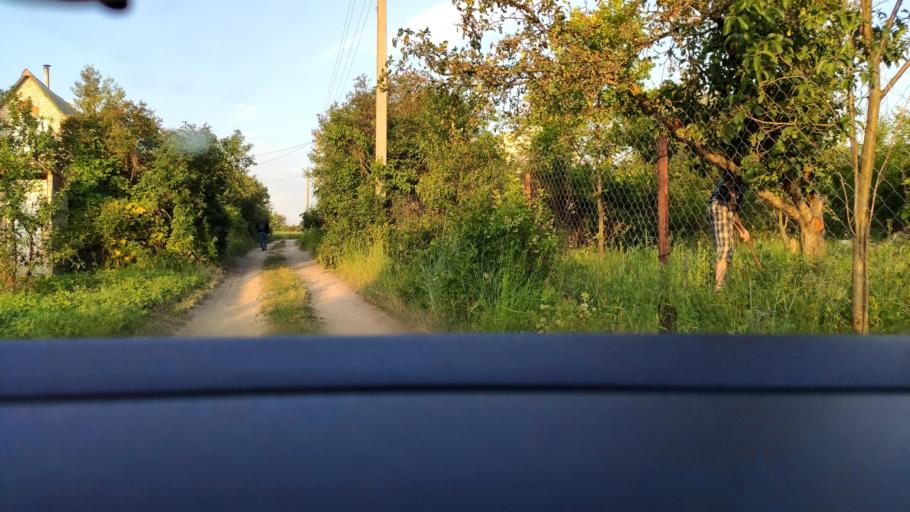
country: RU
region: Voronezj
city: Ramon'
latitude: 51.9119
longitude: 39.1755
